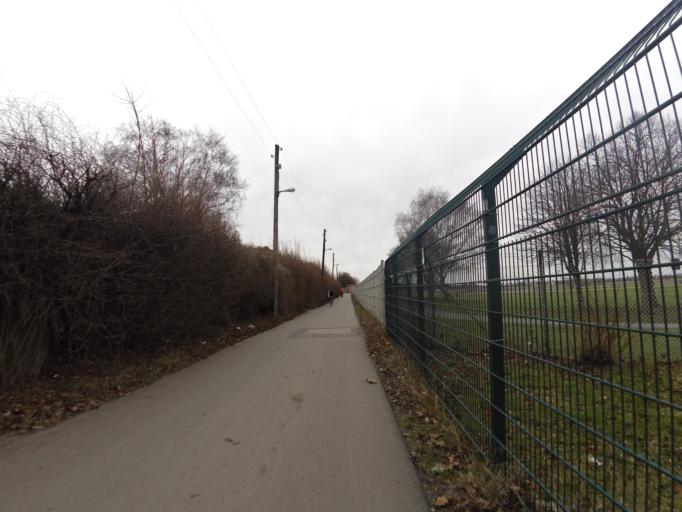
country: DE
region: Berlin
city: Tempelhof Bezirk
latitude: 52.4779
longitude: 13.4180
